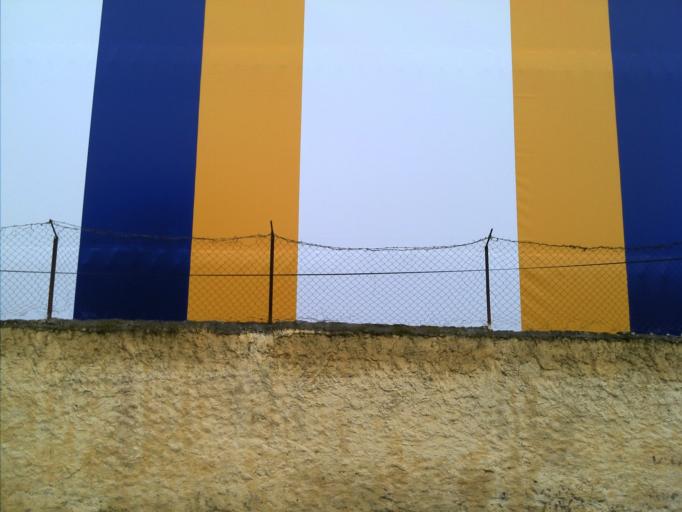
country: AL
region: Shkoder
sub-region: Rrethi i Shkodres
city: Shkoder
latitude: 42.0622
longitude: 19.5208
